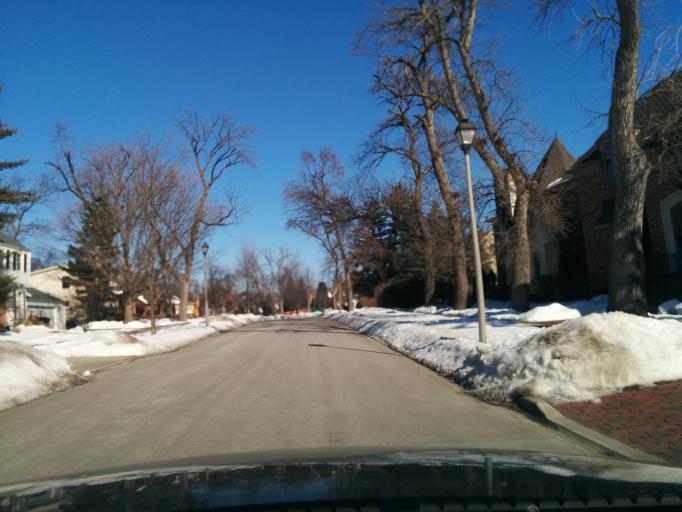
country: US
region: Illinois
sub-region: DuPage County
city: Elmhurst
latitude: 41.8856
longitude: -87.9335
